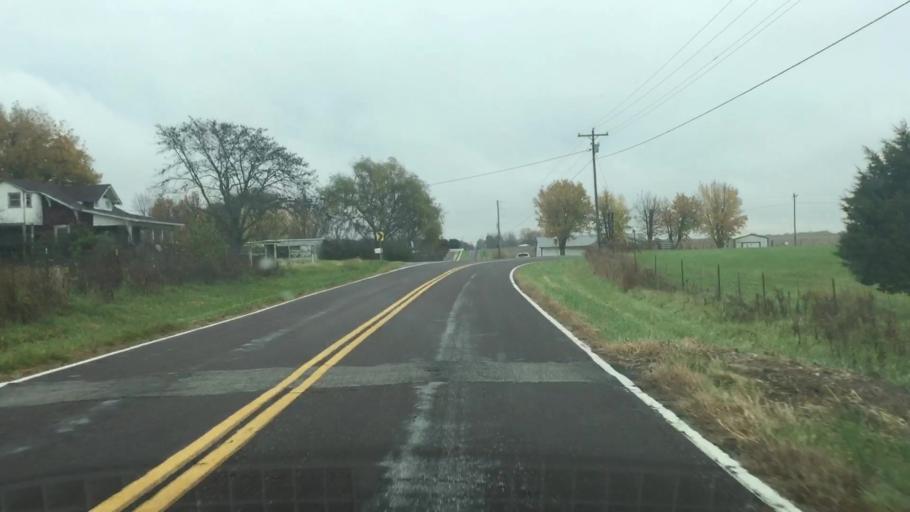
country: US
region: Missouri
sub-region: Callaway County
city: Fulton
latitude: 38.8257
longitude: -91.9099
